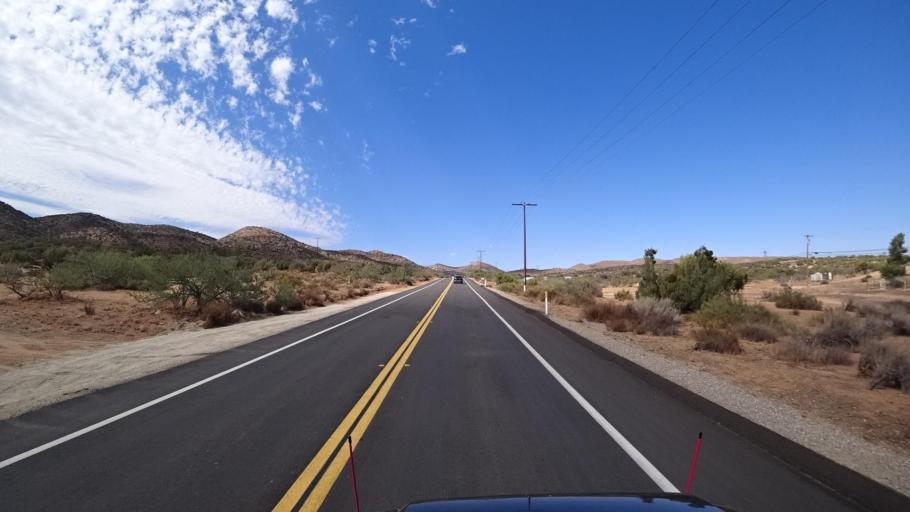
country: MX
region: Baja California
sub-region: Tecate
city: Cereso del Hongo
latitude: 32.6281
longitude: -116.2229
